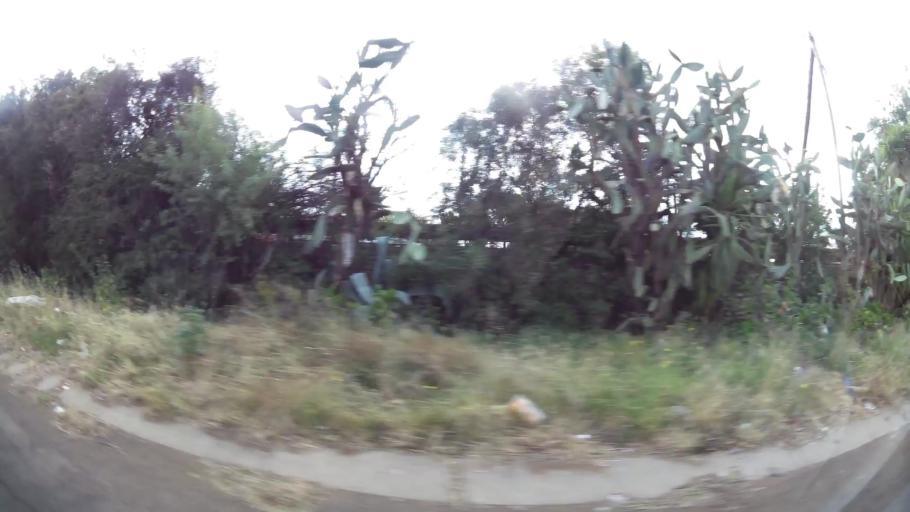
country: ZA
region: Orange Free State
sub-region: Mangaung Metropolitan Municipality
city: Bloemfontein
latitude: -29.0815
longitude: 26.1959
